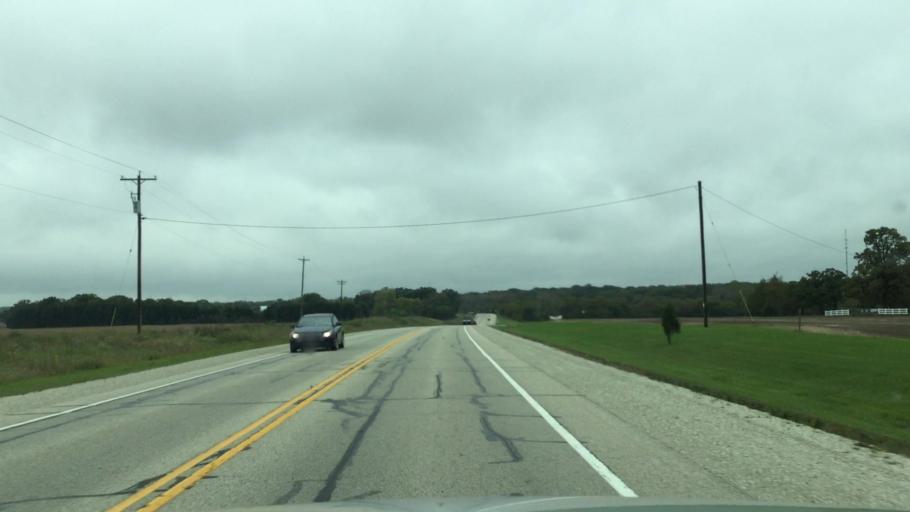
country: US
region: Wisconsin
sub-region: Racine County
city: Eagle Lake
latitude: 42.7418
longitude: -88.1367
